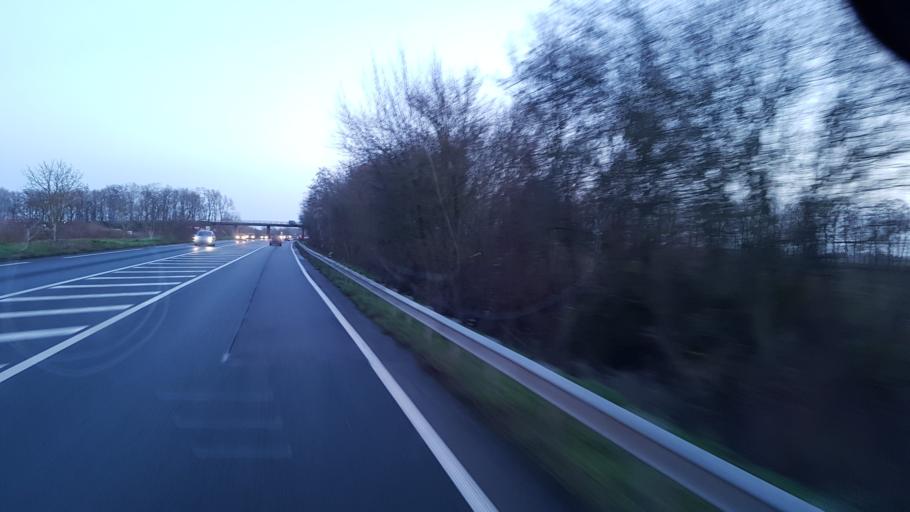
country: FR
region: Nord-Pas-de-Calais
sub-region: Departement du Nord
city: Lambres-lez-Douai
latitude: 50.3440
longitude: 3.0754
